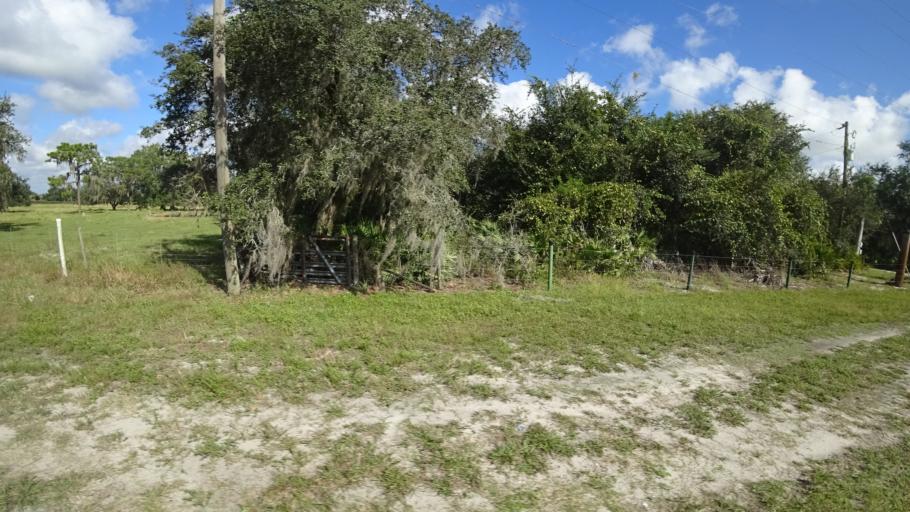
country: US
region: Florida
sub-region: Sarasota County
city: Lake Sarasota
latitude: 27.3391
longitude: -82.1949
